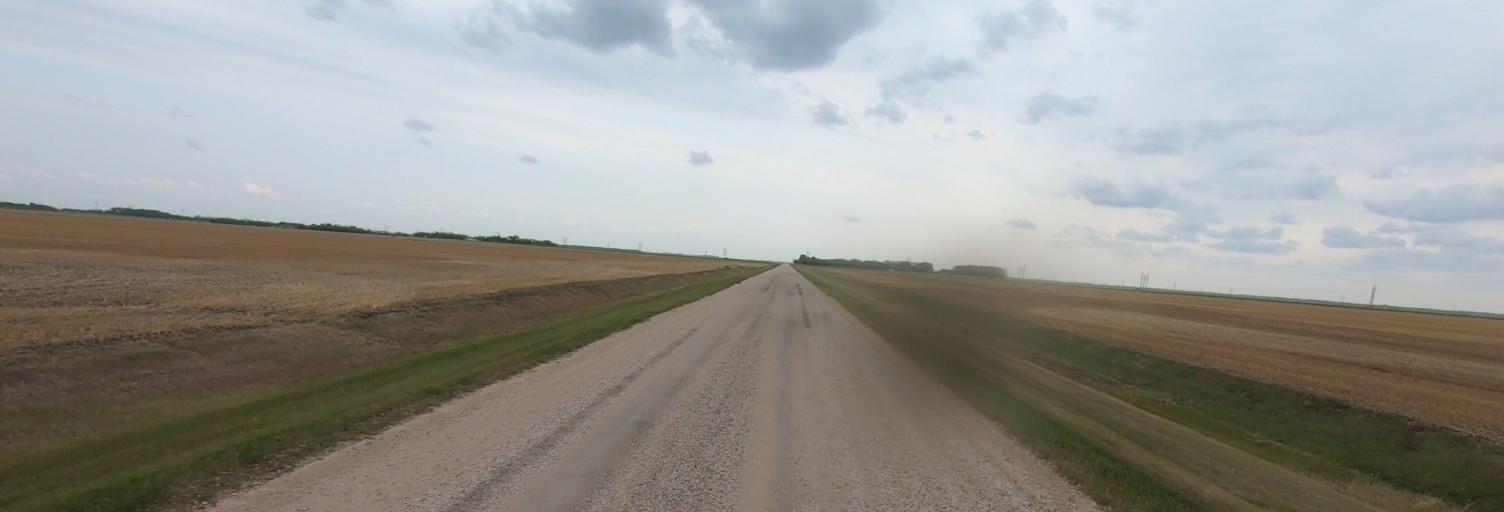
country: CA
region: Manitoba
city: Headingley
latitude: 49.7242
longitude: -97.3839
